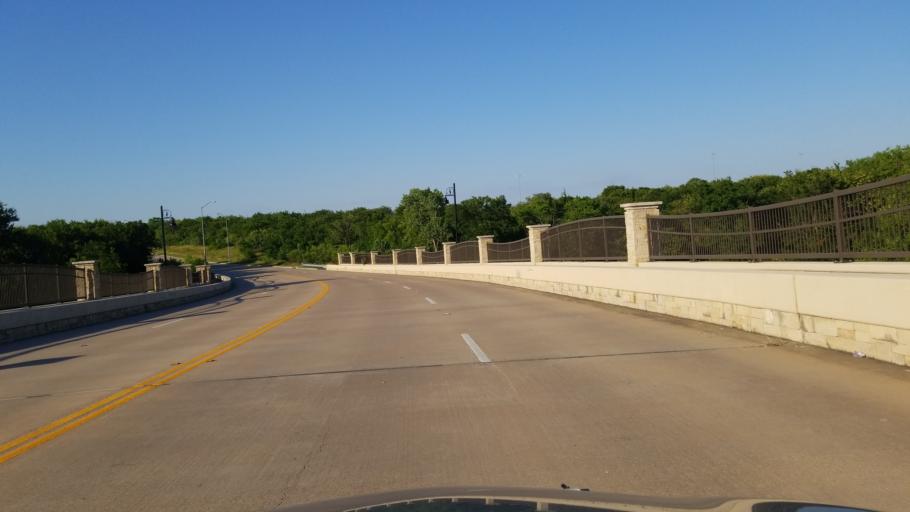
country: US
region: Texas
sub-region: Dallas County
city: Grand Prairie
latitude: 32.6779
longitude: -97.0310
